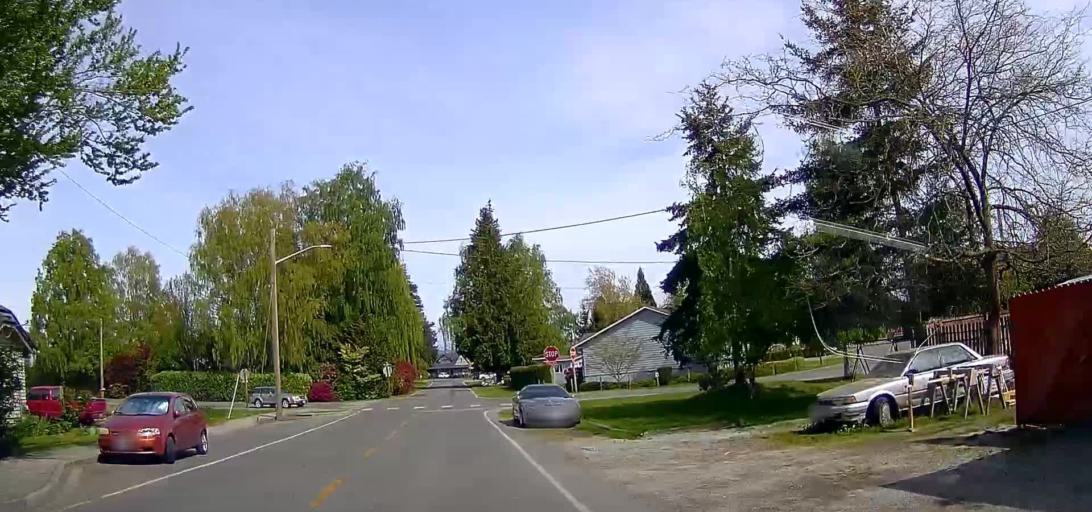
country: US
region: Washington
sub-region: Skagit County
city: Mount Vernon
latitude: 48.3912
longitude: -122.4930
